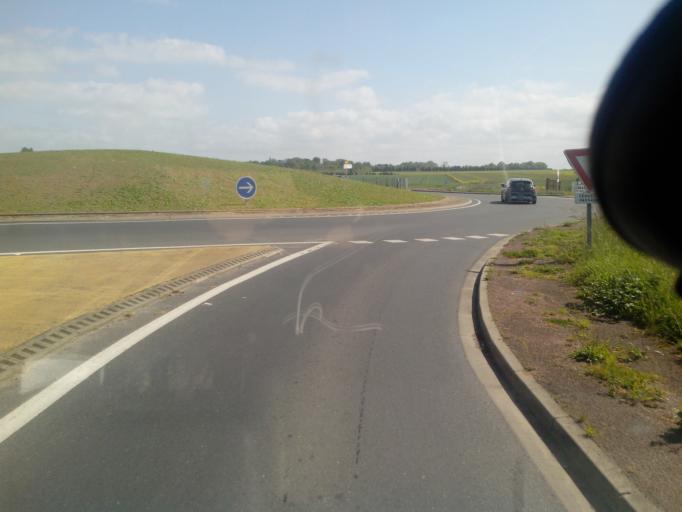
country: FR
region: Lower Normandy
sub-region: Departement du Calvados
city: Bernieres-sur-Mer
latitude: 49.3037
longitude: -0.4377
